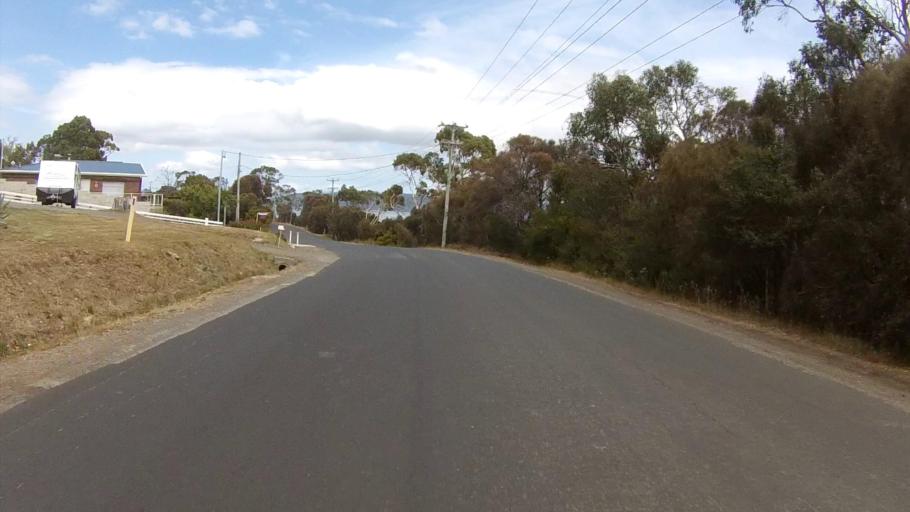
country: AU
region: Tasmania
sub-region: Kingborough
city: Margate
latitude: -43.0248
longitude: 147.2908
